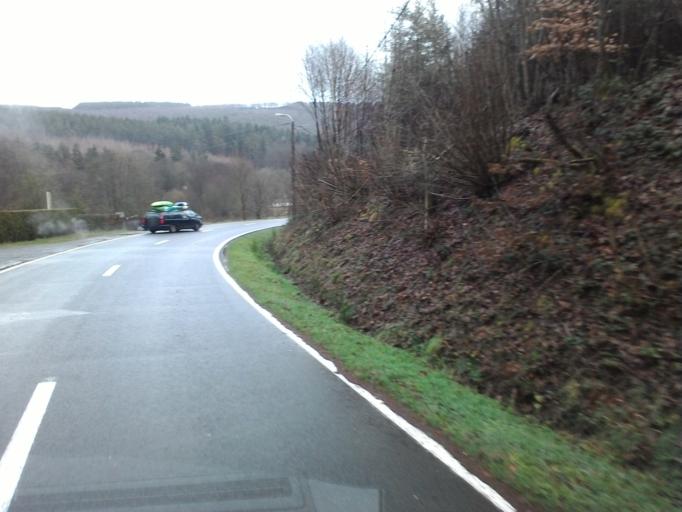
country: BE
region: Wallonia
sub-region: Province de Liege
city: Stoumont
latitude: 50.4105
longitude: 5.7694
